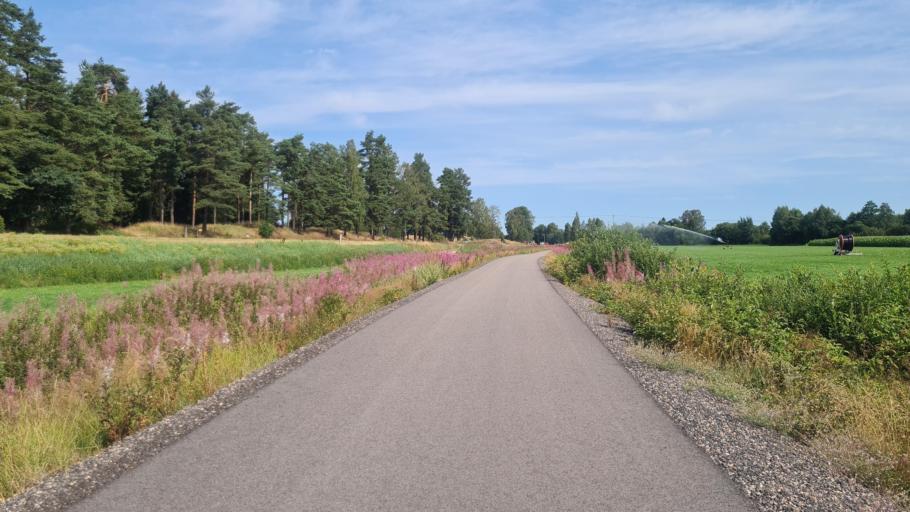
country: SE
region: Kronoberg
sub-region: Ljungby Kommun
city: Ljungby
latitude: 56.8671
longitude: 13.9773
